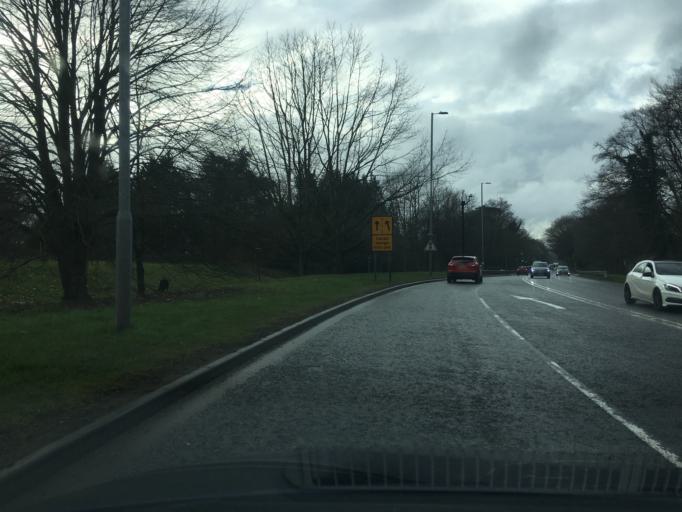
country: GB
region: England
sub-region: Bracknell Forest
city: Bracknell
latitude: 51.4089
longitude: -0.7514
